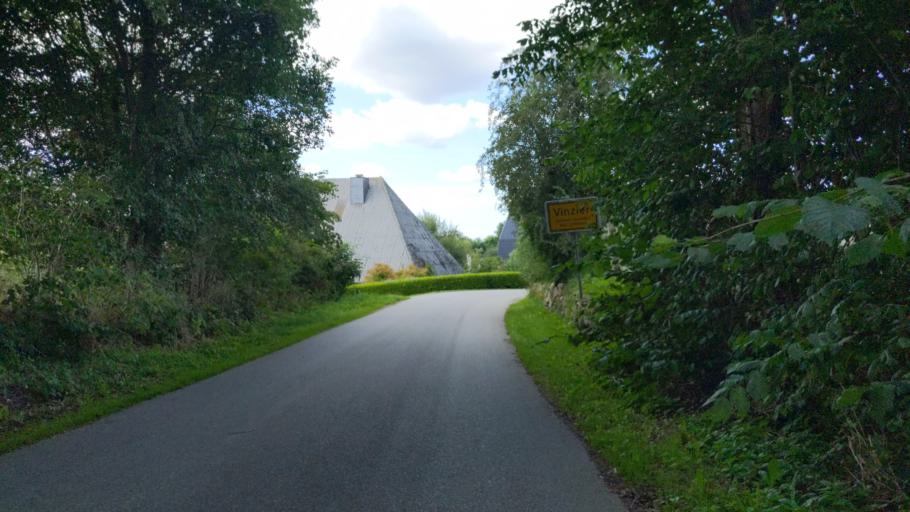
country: DE
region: Schleswig-Holstein
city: Kasseedorf
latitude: 54.1207
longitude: 10.7127
